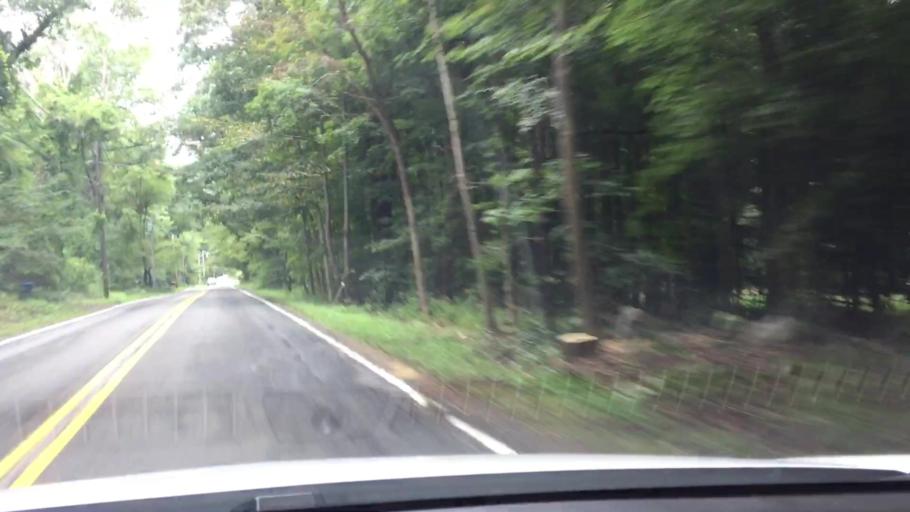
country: US
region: Massachusetts
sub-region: Berkshire County
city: Housatonic
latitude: 42.2360
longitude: -73.3706
